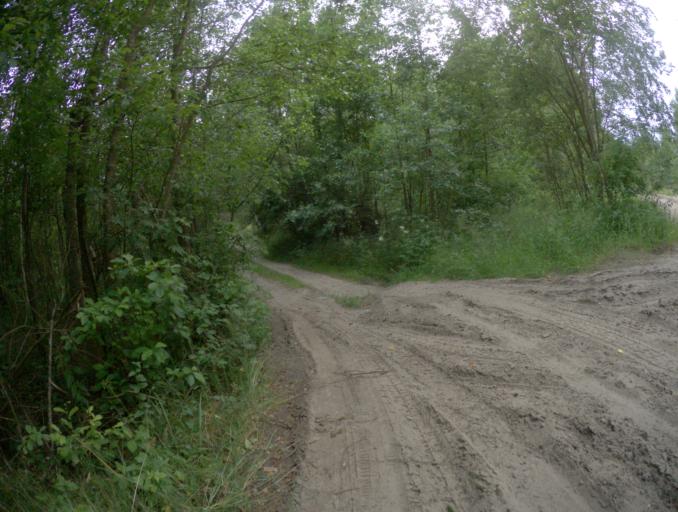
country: RU
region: Nizjnij Novgorod
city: Frolishchi
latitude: 56.4538
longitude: 42.6823
